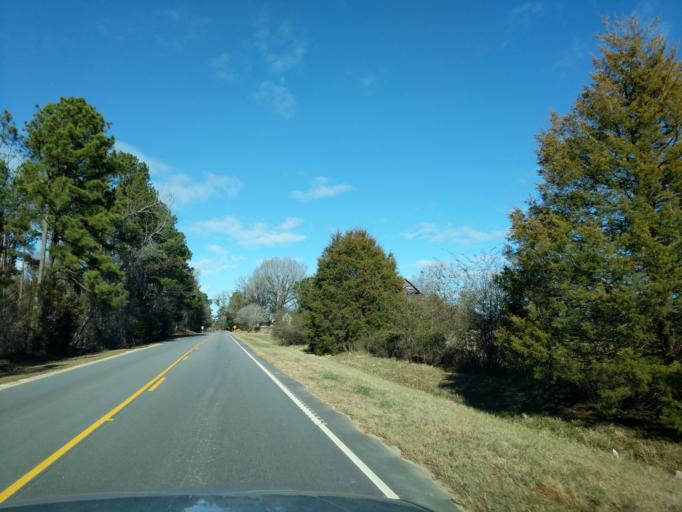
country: US
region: South Carolina
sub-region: Edgefield County
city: Edgefield
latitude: 33.9453
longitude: -82.0476
